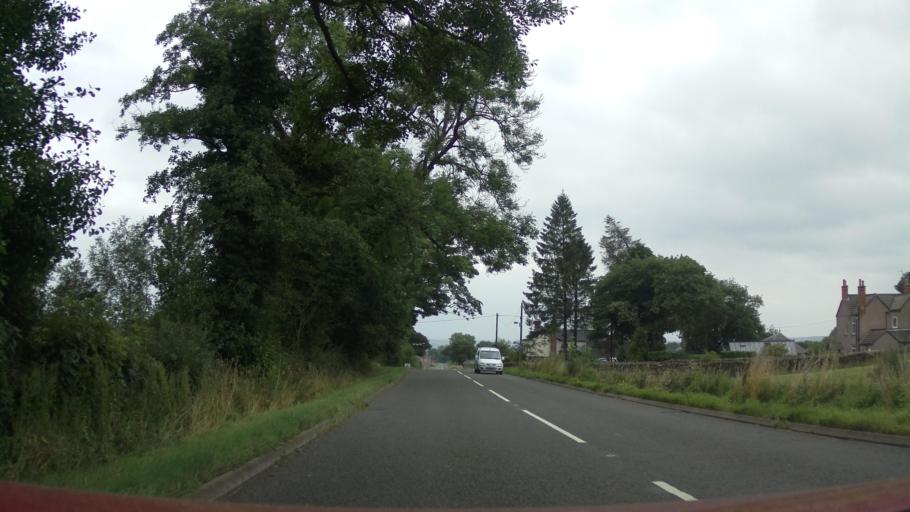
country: GB
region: England
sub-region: Staffordshire
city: Cheadle
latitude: 53.0295
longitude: -1.9294
